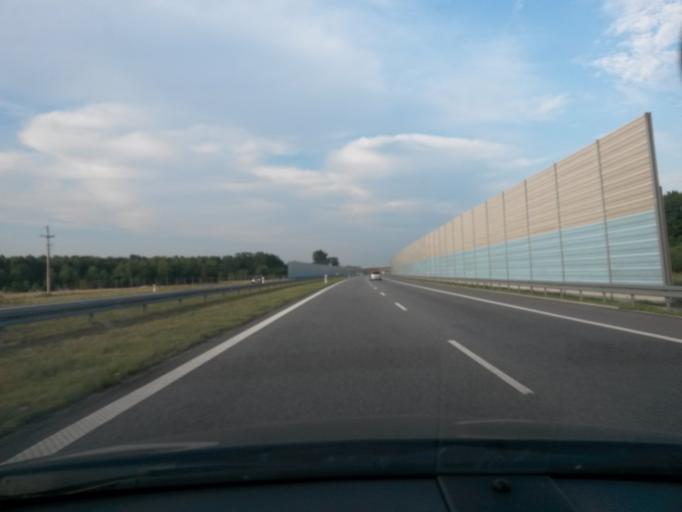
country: PL
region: Lodz Voivodeship
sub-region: powiat Lowicki
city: Lyszkowice
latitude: 52.0140
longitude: 19.9659
